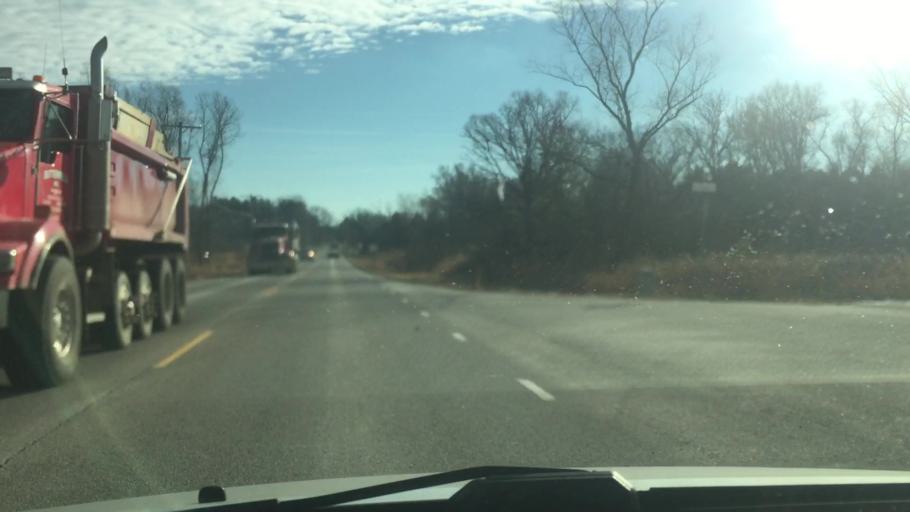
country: US
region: Wisconsin
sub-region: Waukesha County
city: Delafield
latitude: 43.0461
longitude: -88.4044
